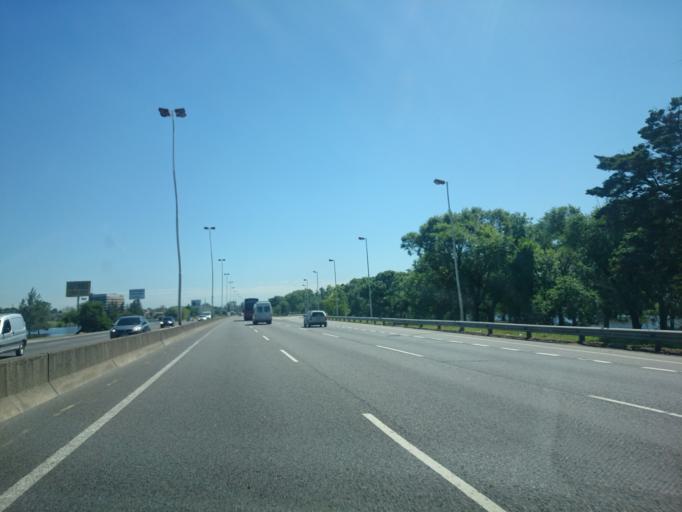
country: AR
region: Buenos Aires
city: San Justo
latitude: -34.7401
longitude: -58.5203
